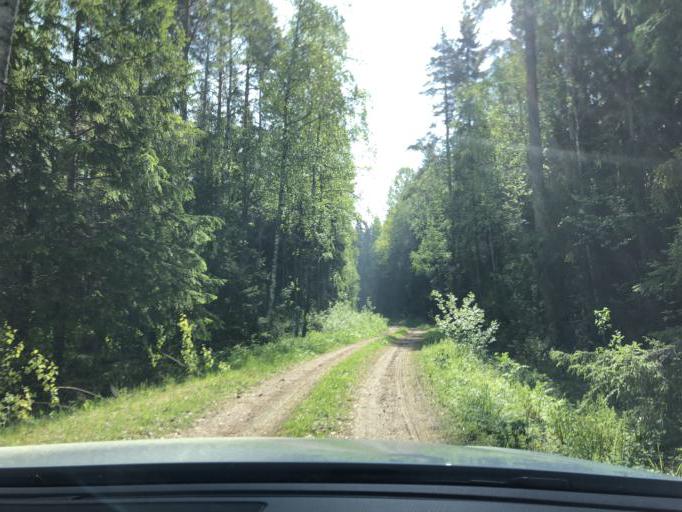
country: SE
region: Dalarna
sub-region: Avesta Kommun
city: Horndal
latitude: 60.2162
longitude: 16.4969
